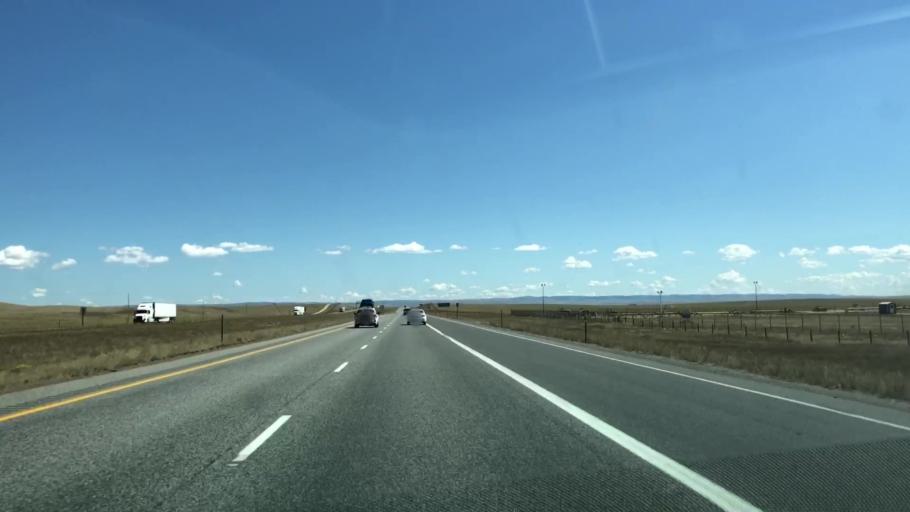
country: US
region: Wyoming
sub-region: Albany County
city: Laramie
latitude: 41.4396
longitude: -105.9379
